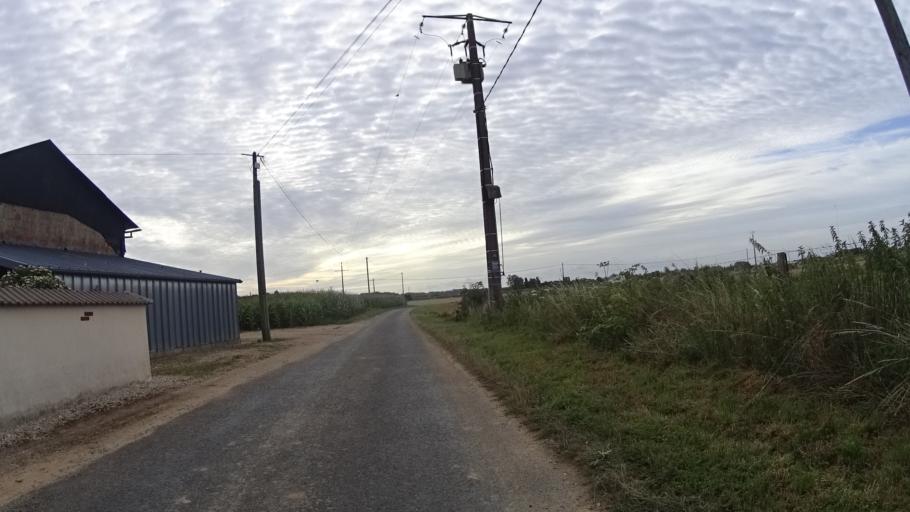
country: FR
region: Centre
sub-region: Departement du Loiret
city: Saint-Benoit-sur-Loire
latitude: 47.8436
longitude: 2.2844
